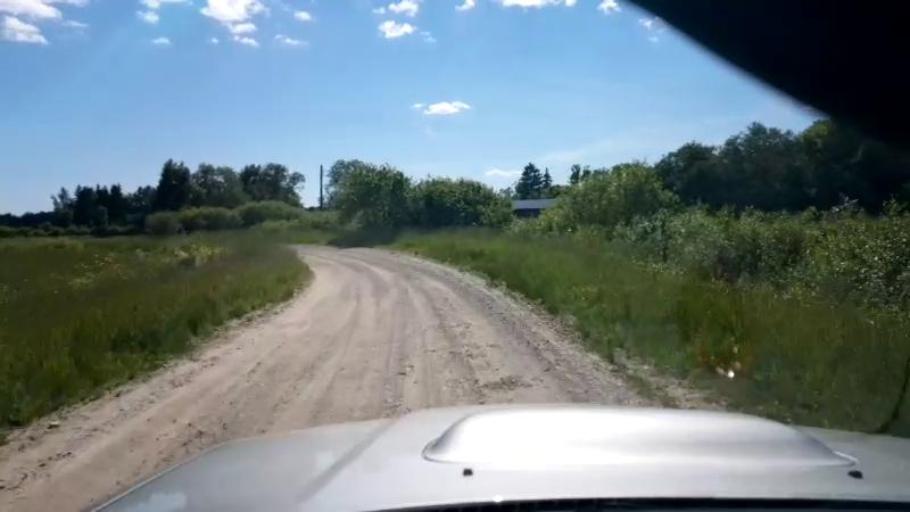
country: EE
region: Paernumaa
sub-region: Sauga vald
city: Sauga
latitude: 58.5107
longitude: 24.5138
